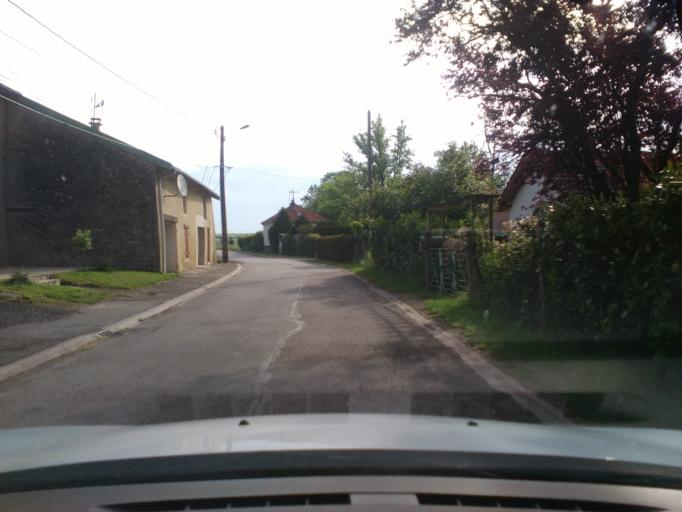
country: FR
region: Lorraine
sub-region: Departement des Vosges
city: Mirecourt
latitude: 48.3484
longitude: 6.1492
